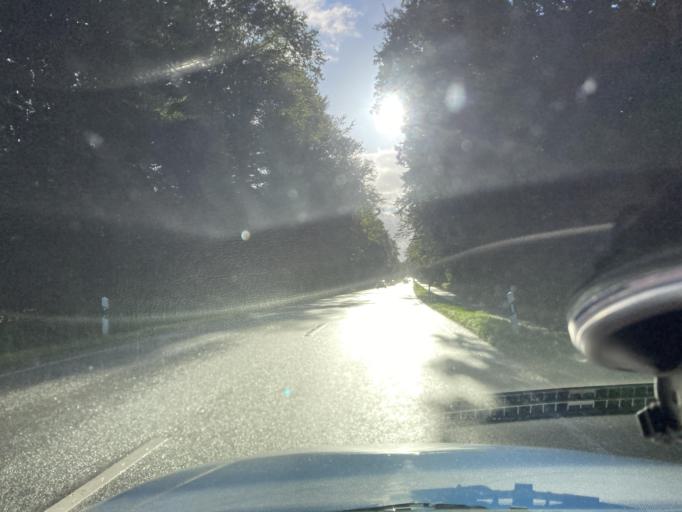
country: DE
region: Schleswig-Holstein
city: Fockbek
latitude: 54.2738
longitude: 9.5691
